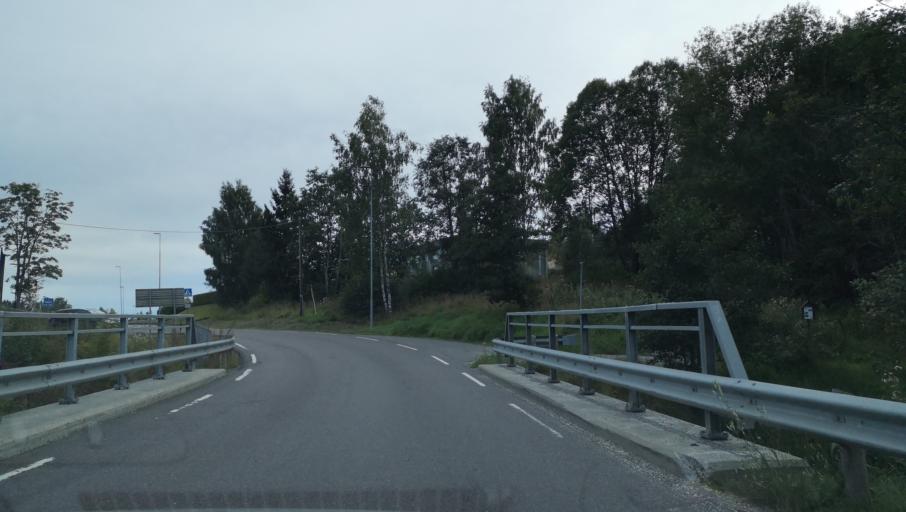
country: NO
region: Ostfold
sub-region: Hobol
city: Tomter
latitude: 59.7223
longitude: 11.0553
